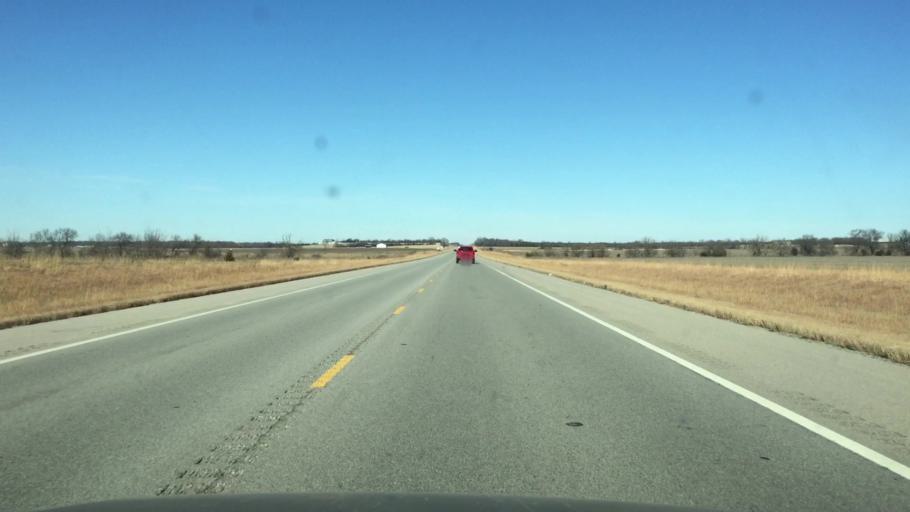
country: US
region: Kansas
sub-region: Allen County
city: Iola
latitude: 37.9550
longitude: -95.3812
